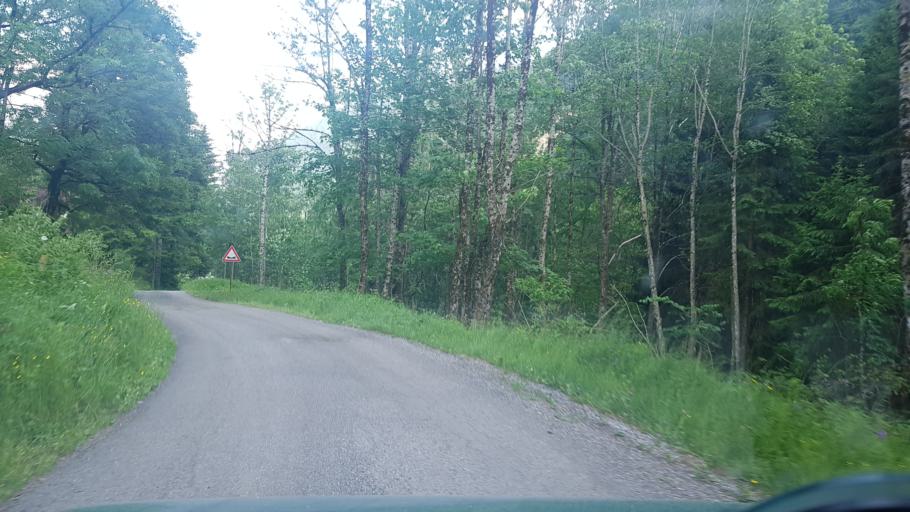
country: IT
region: Friuli Venezia Giulia
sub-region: Provincia di Udine
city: Pontebba
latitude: 46.5268
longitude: 13.2159
